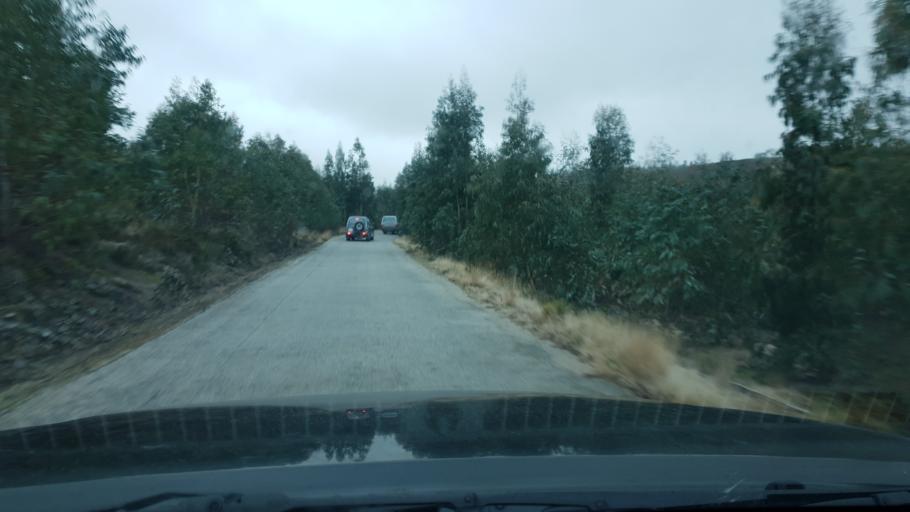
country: PT
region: Viseu
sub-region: Sao Pedro do Sul
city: Sao Pedro do Sul
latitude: 40.8657
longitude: -8.0901
